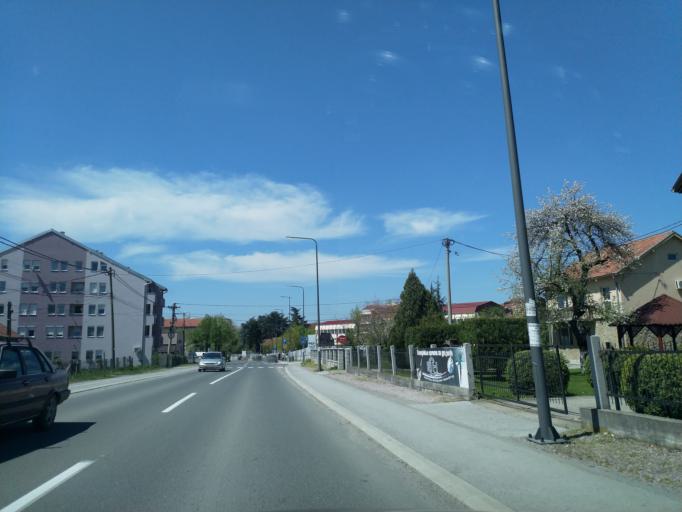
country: RS
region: Central Serbia
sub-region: Belgrade
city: Lazarevac
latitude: 44.3806
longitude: 20.2775
